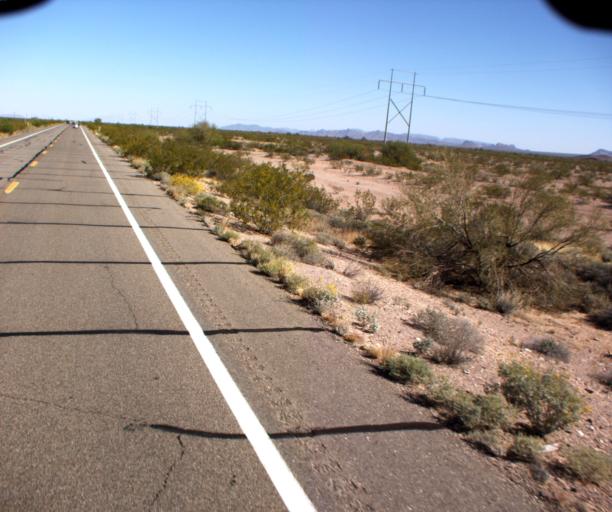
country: US
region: Arizona
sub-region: La Paz County
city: Quartzsite
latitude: 33.3243
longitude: -114.2169
